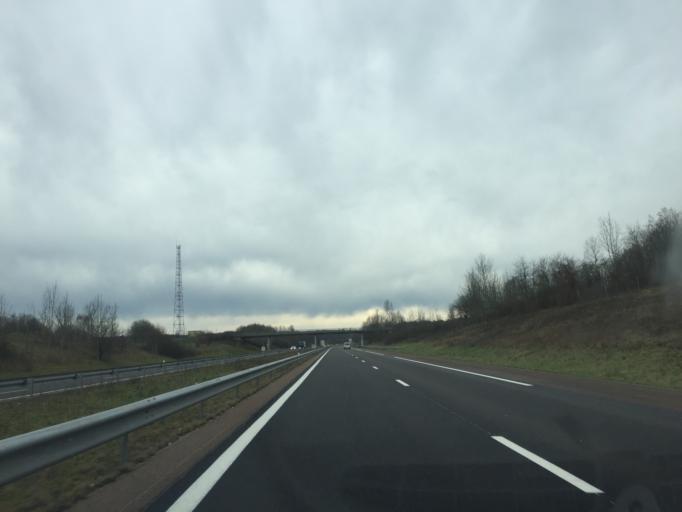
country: FR
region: Franche-Comte
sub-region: Departement du Jura
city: Bletterans
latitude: 46.8062
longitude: 5.5333
